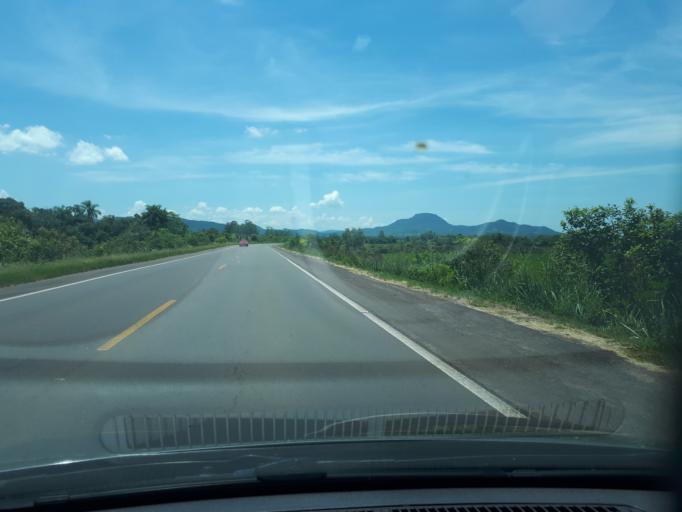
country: BR
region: Rio Grande do Sul
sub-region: Candelaria
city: Candelaria
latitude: -29.7305
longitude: -52.9435
